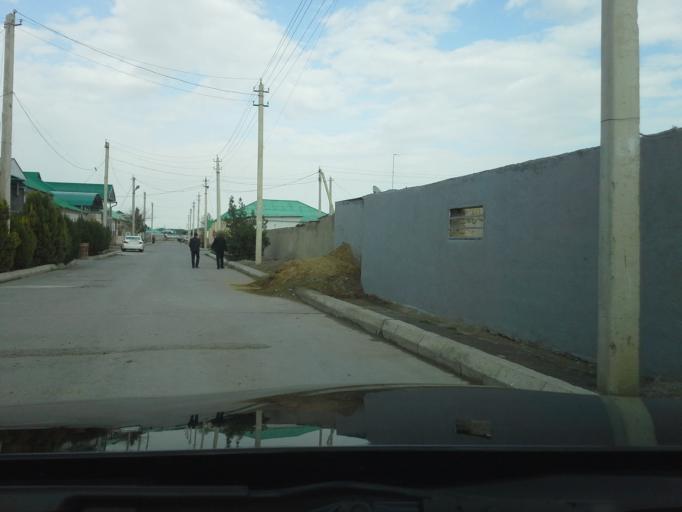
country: TM
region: Ahal
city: Abadan
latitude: 37.9905
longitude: 58.2826
